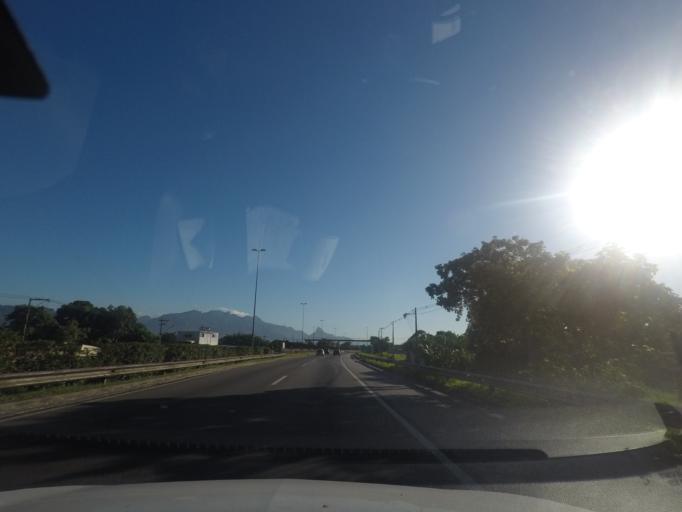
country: BR
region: Rio de Janeiro
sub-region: Duque De Caxias
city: Duque de Caxias
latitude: -22.6523
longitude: -43.2392
